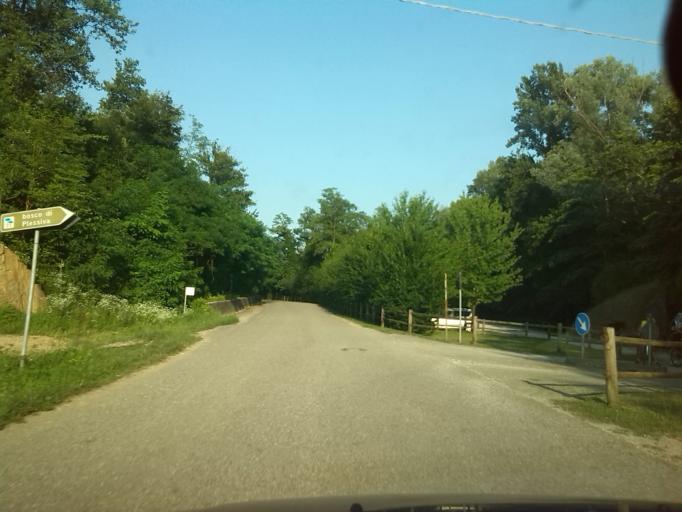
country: IT
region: Friuli Venezia Giulia
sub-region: Provincia di Gorizia
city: Cormons
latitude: 45.9853
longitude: 13.4848
